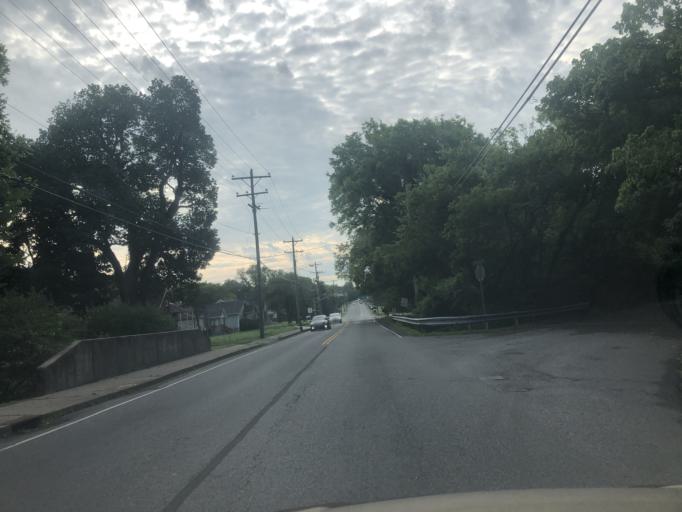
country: US
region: Tennessee
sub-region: Davidson County
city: Goodlettsville
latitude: 36.2558
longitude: -86.7092
